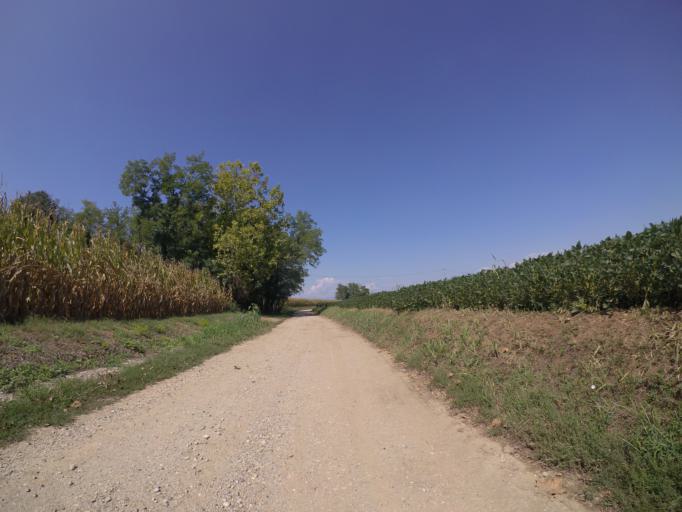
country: IT
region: Friuli Venezia Giulia
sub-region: Provincia di Udine
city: Bertiolo
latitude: 45.9410
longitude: 13.0694
